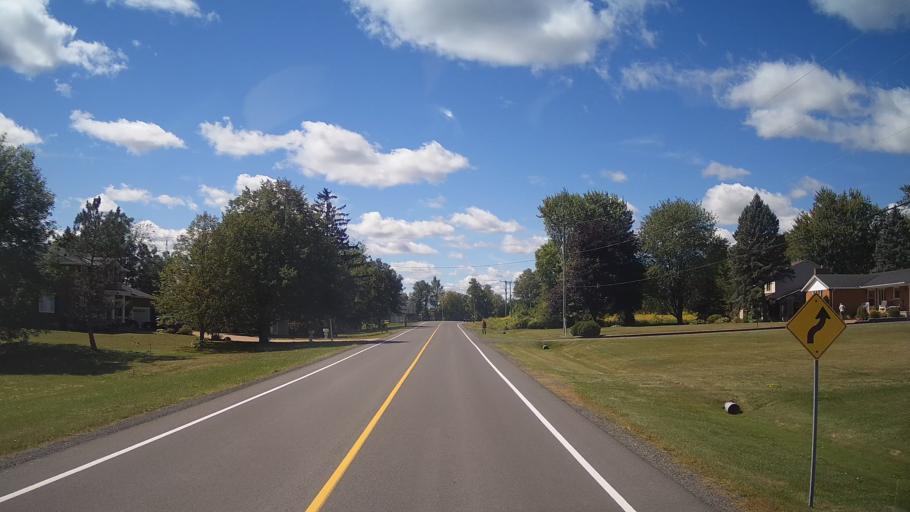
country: US
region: New York
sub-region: St. Lawrence County
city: Norfolk
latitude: 44.8638
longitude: -75.2549
